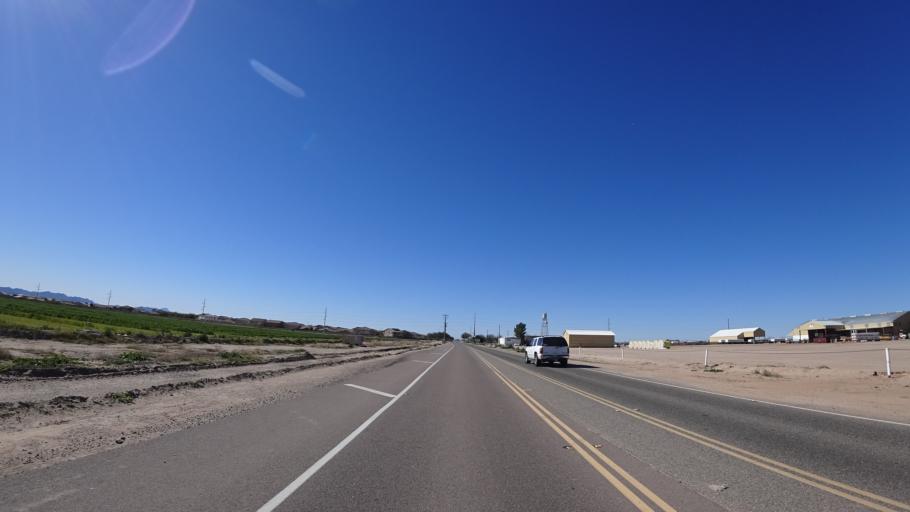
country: US
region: Arizona
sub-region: Maricopa County
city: Buckeye
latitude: 33.3919
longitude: -112.5964
